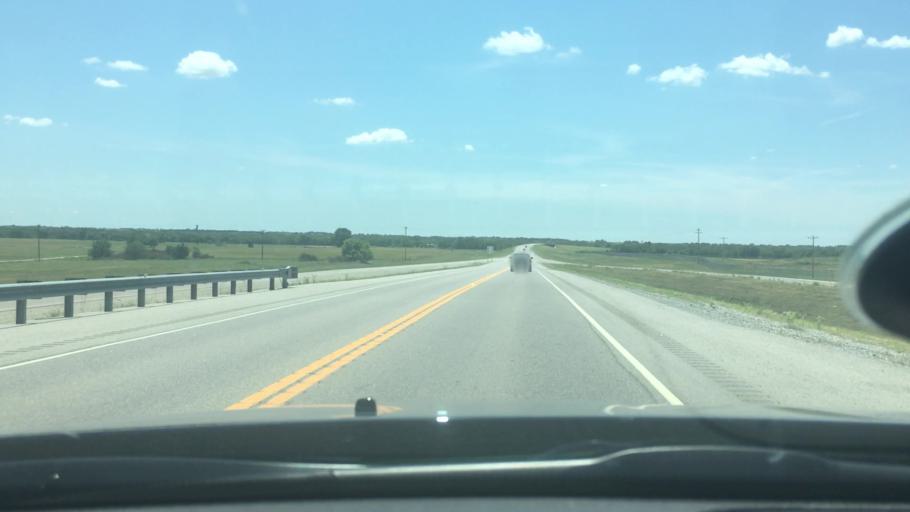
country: US
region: Oklahoma
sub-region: Bryan County
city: Durant
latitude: 33.9857
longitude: -96.3397
